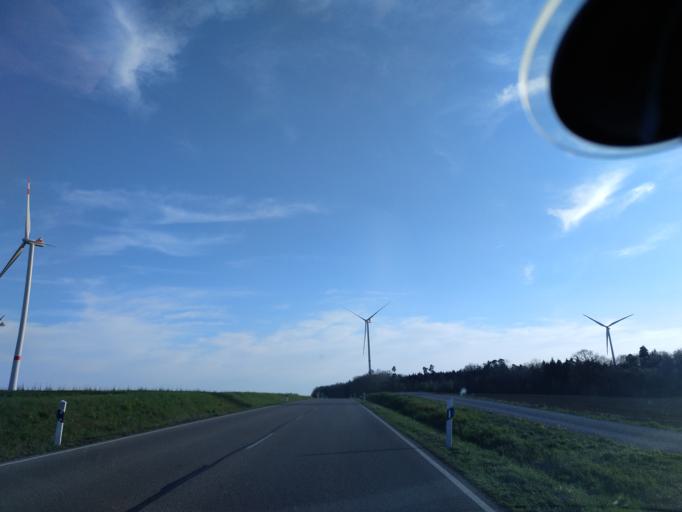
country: DE
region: Baden-Wuerttemberg
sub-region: Regierungsbezirk Stuttgart
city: Kirchberg an der Jagst
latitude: 49.1885
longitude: 9.9691
